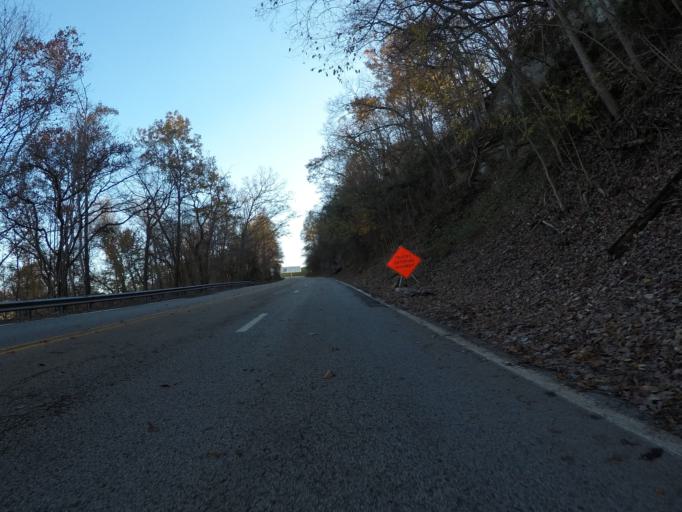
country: US
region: West Virginia
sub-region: Wayne County
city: Ceredo
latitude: 38.3741
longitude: -82.5546
